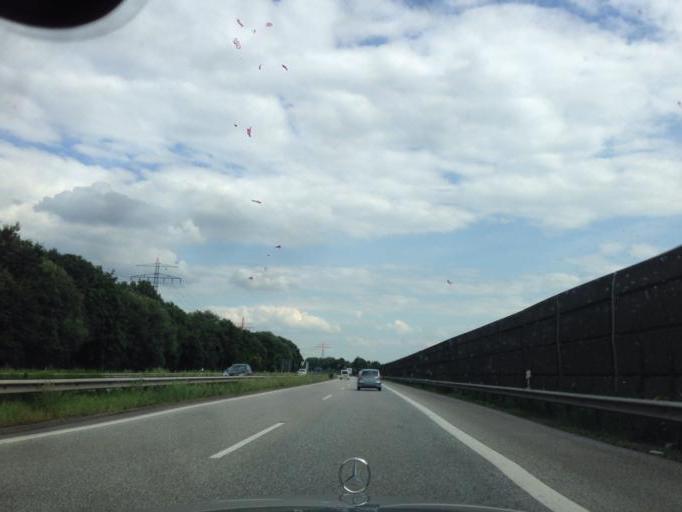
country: DE
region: Hamburg
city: Wandsbek
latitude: 53.4913
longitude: 10.1044
